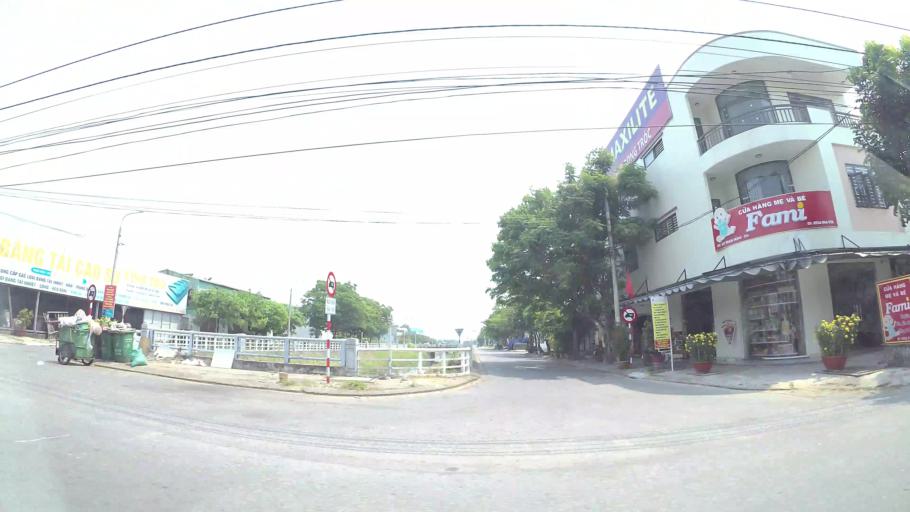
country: VN
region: Da Nang
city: Cam Le
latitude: 15.9900
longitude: 108.2077
